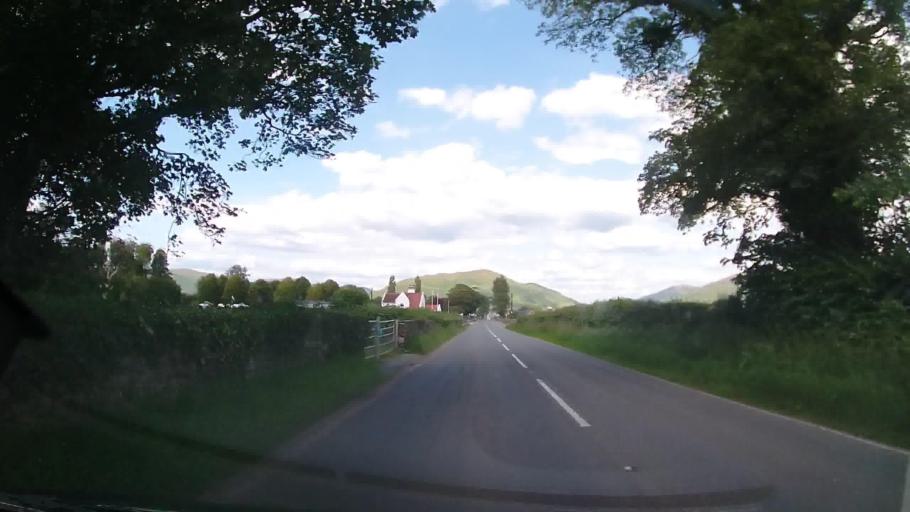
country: GB
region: Wales
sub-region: Gwynedd
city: Tywyn
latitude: 52.5976
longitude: -4.0678
